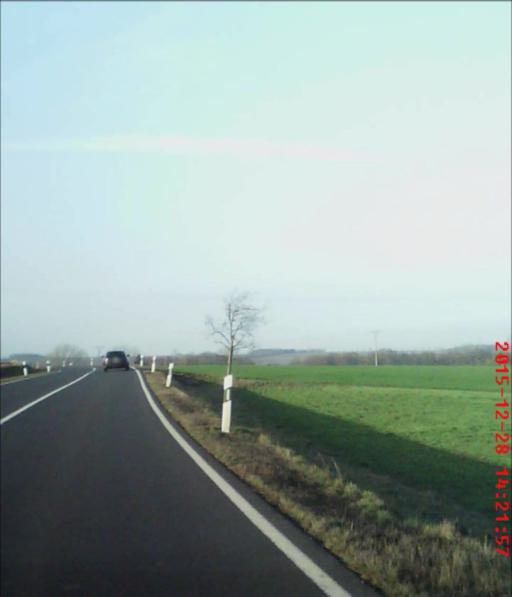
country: DE
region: Thuringia
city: Niederrossla
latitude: 51.0457
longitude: 11.4733
